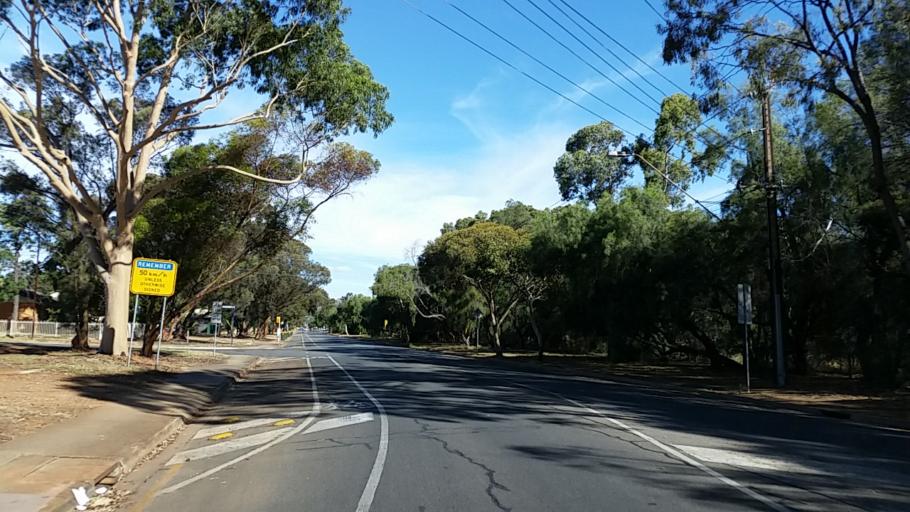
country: AU
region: South Australia
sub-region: Salisbury
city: Salisbury
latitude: -34.7771
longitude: 138.6445
